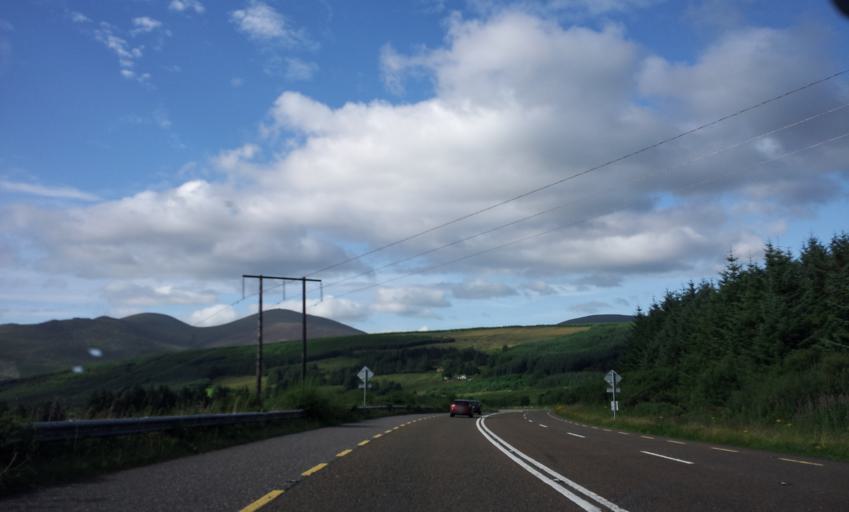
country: IE
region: Munster
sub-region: County Cork
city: Millstreet
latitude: 51.9726
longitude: -9.2528
